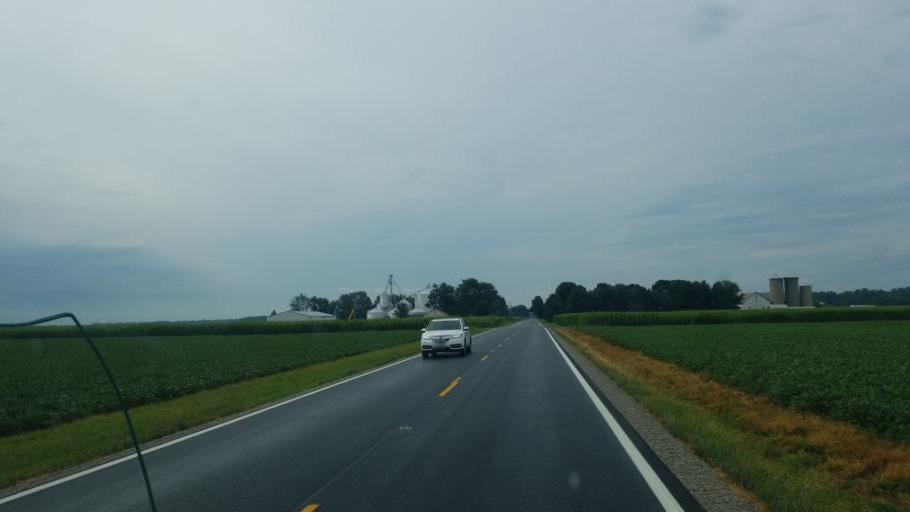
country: US
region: Ohio
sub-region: Williams County
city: Edgerton
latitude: 41.3697
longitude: -84.6696
